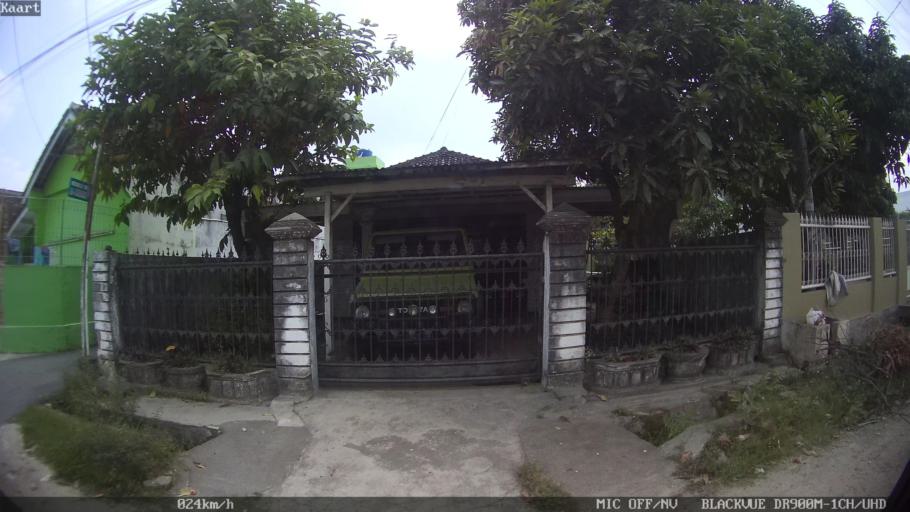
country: ID
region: Lampung
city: Pringsewu
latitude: -5.3501
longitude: 104.9741
